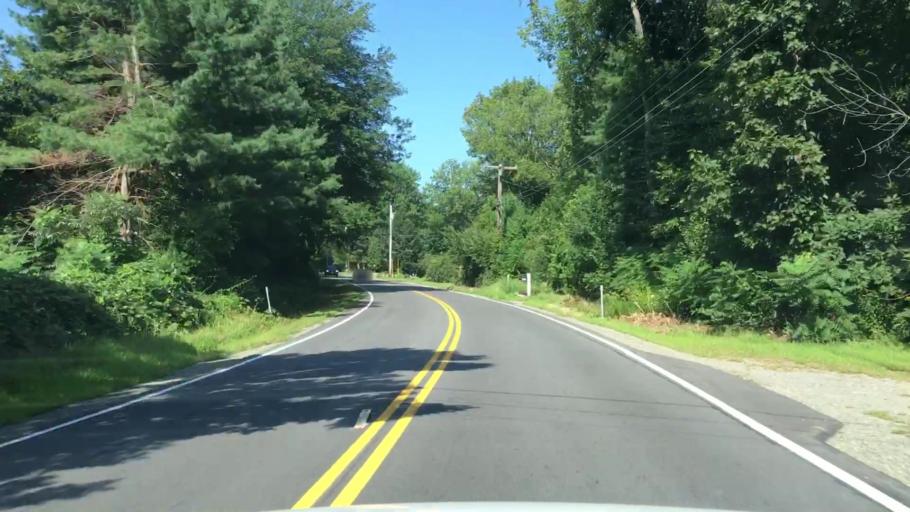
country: US
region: New Hampshire
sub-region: Rockingham County
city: Kensington
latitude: 42.9148
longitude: -70.9687
